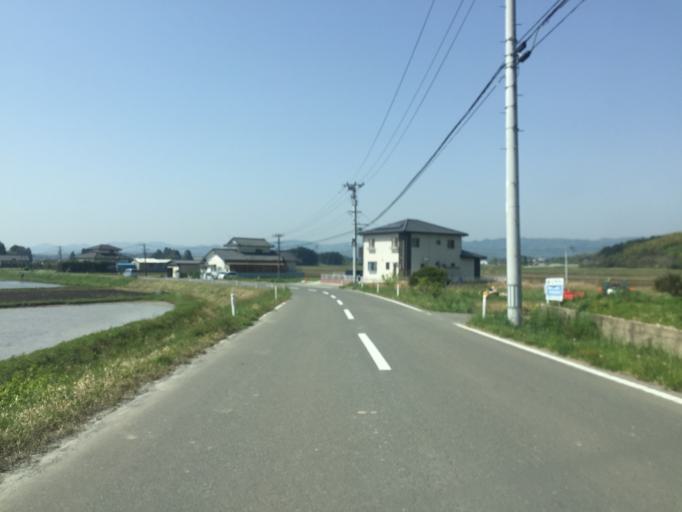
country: JP
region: Miyagi
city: Marumori
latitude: 37.7771
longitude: 140.9570
